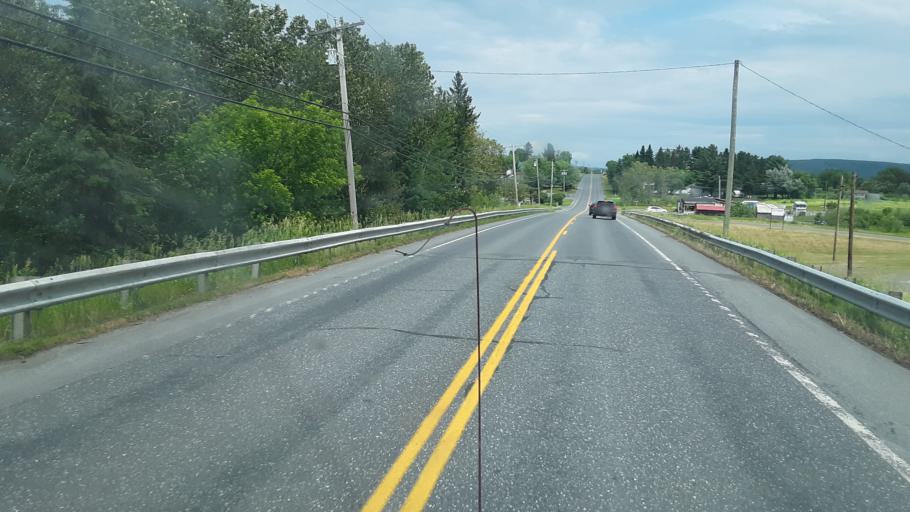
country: US
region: Maine
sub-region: Aroostook County
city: Fort Fairfield
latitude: 46.7633
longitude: -67.8529
